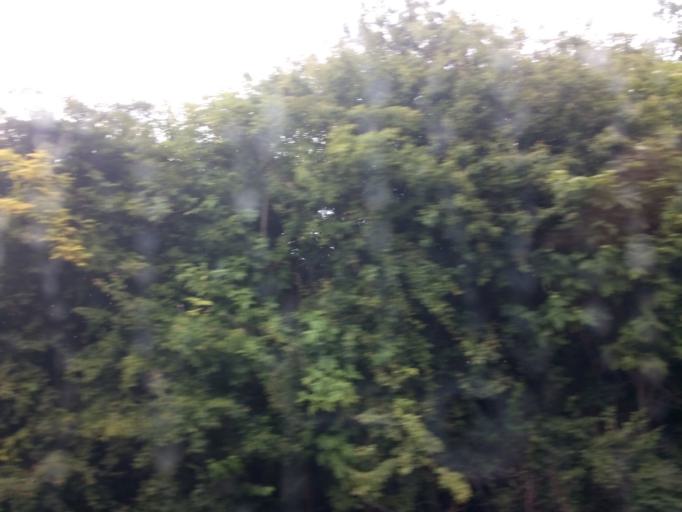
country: GB
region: England
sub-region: South Tyneside
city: Hebburn
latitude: 54.9790
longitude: -1.5132
